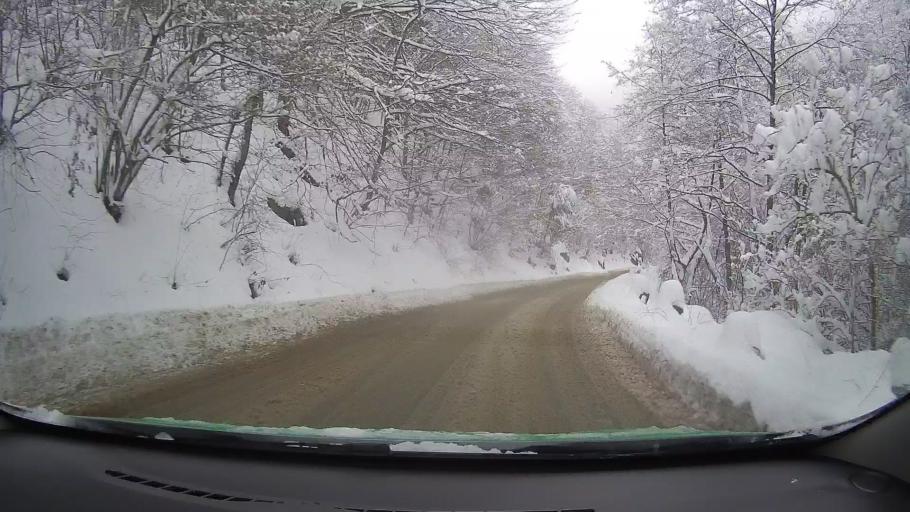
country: RO
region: Sibiu
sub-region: Comuna Tilisca
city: Tilisca
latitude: 45.7992
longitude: 23.8024
